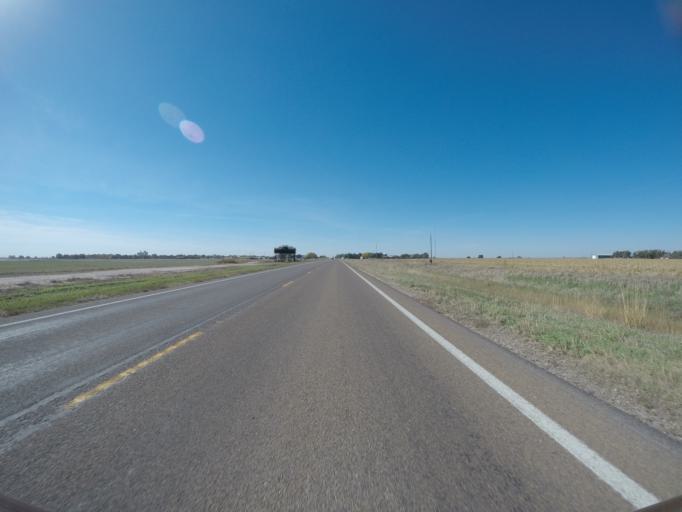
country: US
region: Kansas
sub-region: Smith County
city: Smith Center
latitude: 39.7854
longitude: -98.7635
